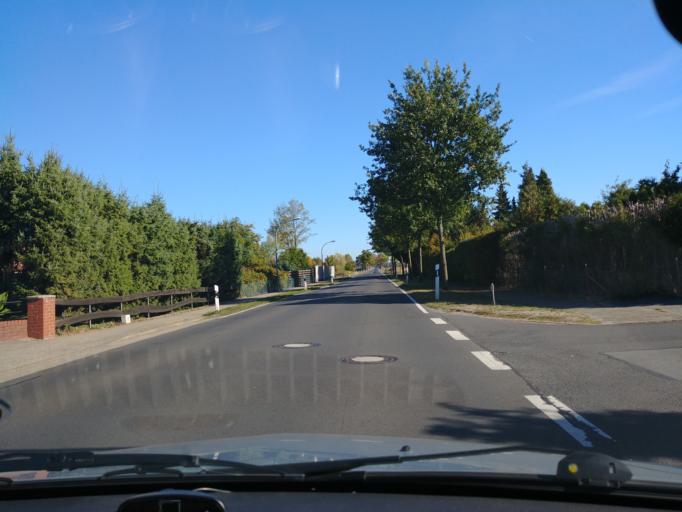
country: DE
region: Lower Saxony
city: Hillerse
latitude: 52.4157
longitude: 10.4090
